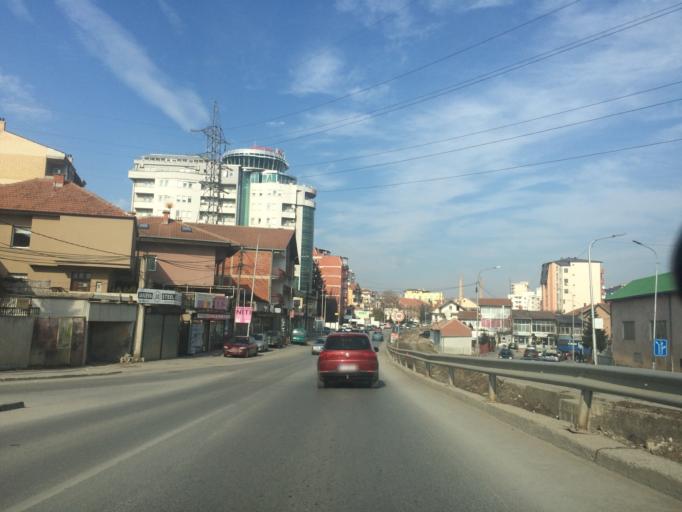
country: XK
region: Pristina
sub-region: Komuna e Prishtines
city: Pristina
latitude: 42.6643
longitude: 21.1550
